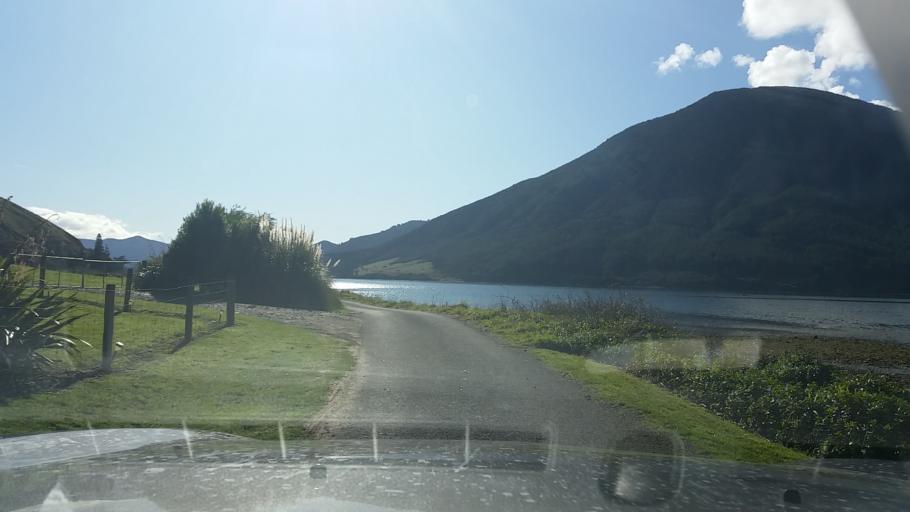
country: NZ
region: Marlborough
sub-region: Marlborough District
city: Picton
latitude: -41.1128
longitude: 174.0346
